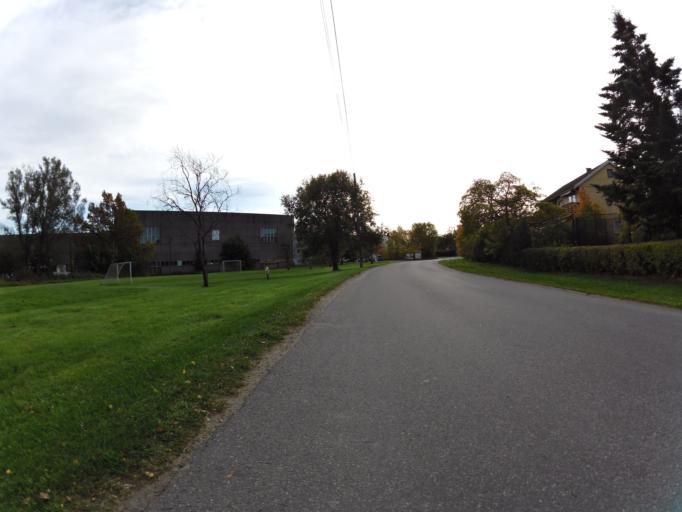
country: NO
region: Ostfold
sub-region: Fredrikstad
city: Fredrikstad
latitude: 59.2190
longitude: 10.9114
